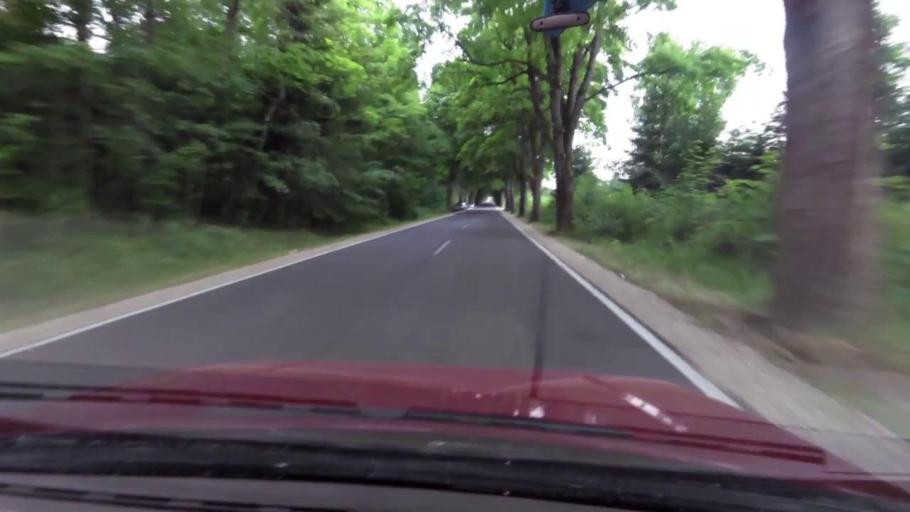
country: PL
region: West Pomeranian Voivodeship
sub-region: Powiat koszalinski
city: Sianow
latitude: 54.1538
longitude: 16.4639
